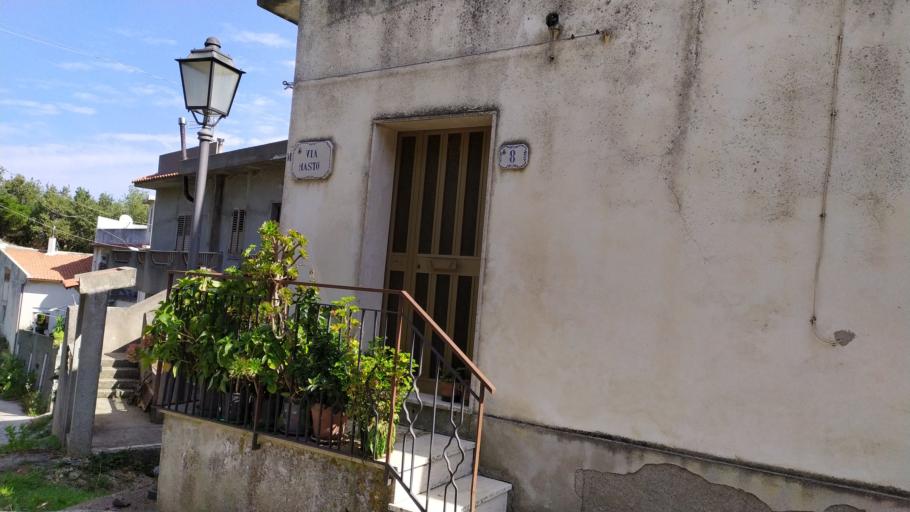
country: IT
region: Sicily
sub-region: Messina
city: Rometta
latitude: 38.1627
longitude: 15.4183
